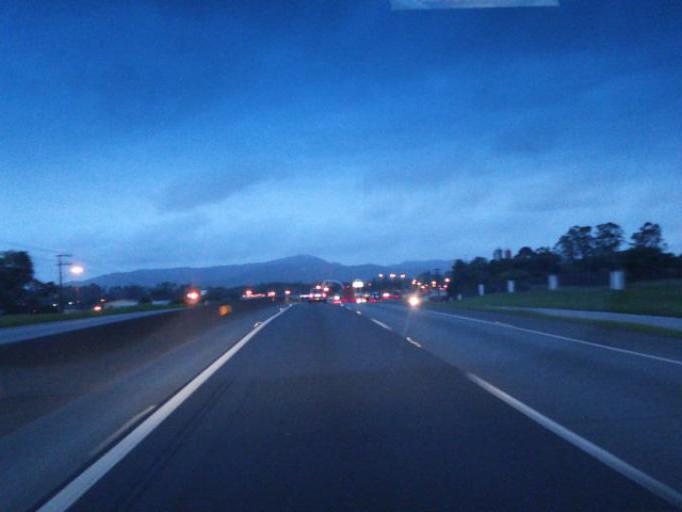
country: BR
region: Santa Catarina
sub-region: Penha
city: Penha
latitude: -26.7594
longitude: -48.6875
